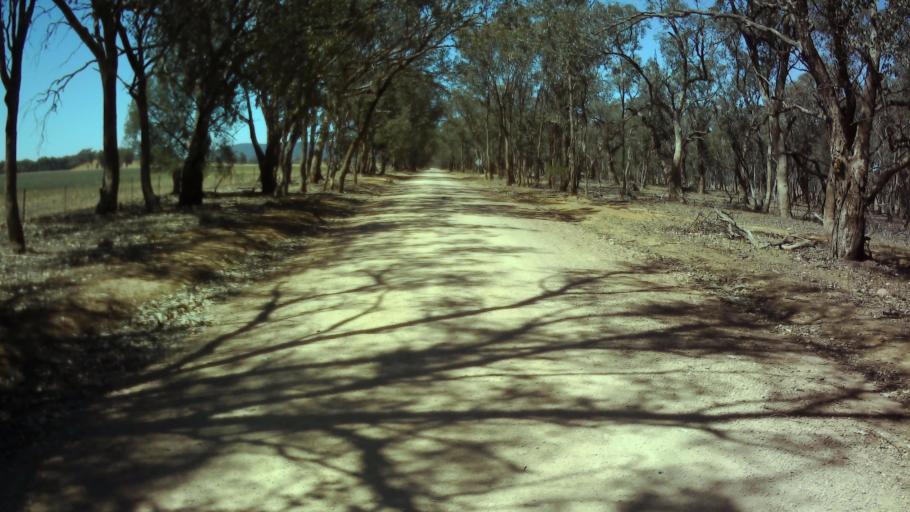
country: AU
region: New South Wales
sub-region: Weddin
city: Grenfell
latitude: -33.9082
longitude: 148.0802
